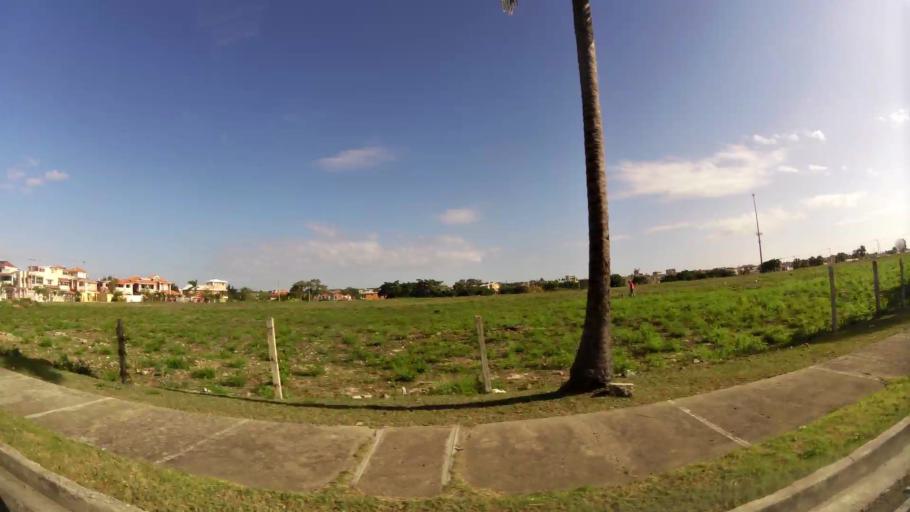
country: DO
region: Santo Domingo
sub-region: Santo Domingo
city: Santo Domingo Este
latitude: 18.4694
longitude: -69.8579
